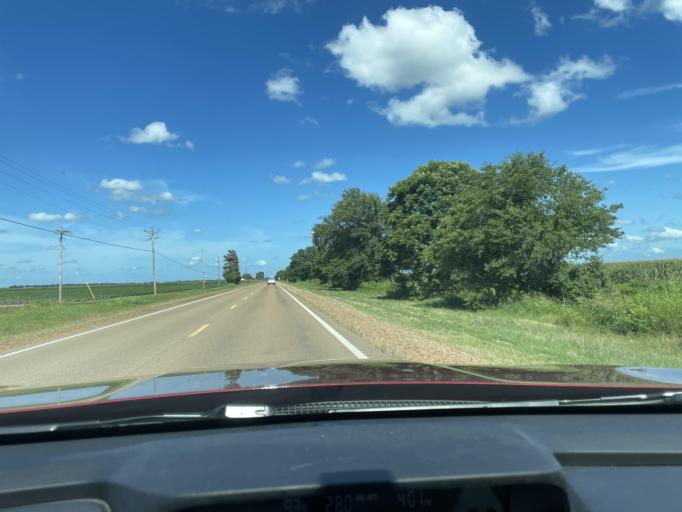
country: US
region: Mississippi
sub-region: Humphreys County
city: Belzoni
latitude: 33.1837
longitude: -90.5366
